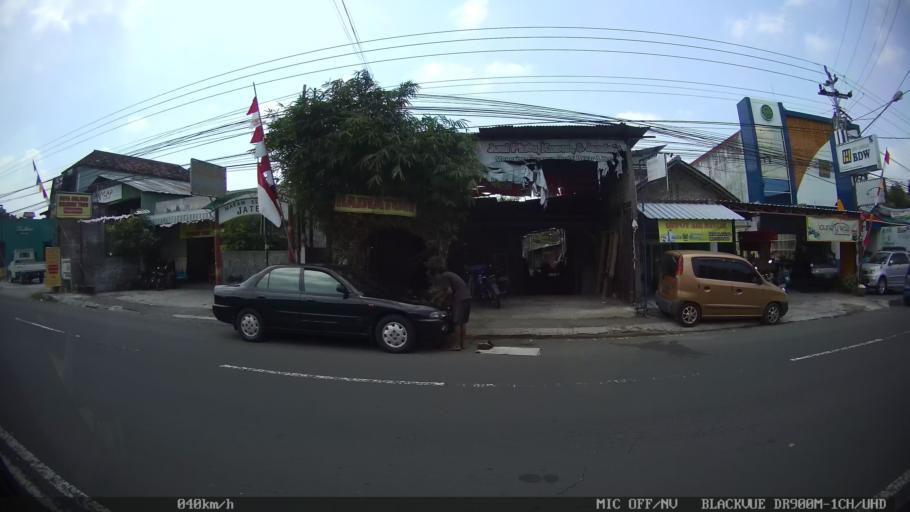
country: ID
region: Daerah Istimewa Yogyakarta
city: Yogyakarta
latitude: -7.8156
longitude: 110.4022
